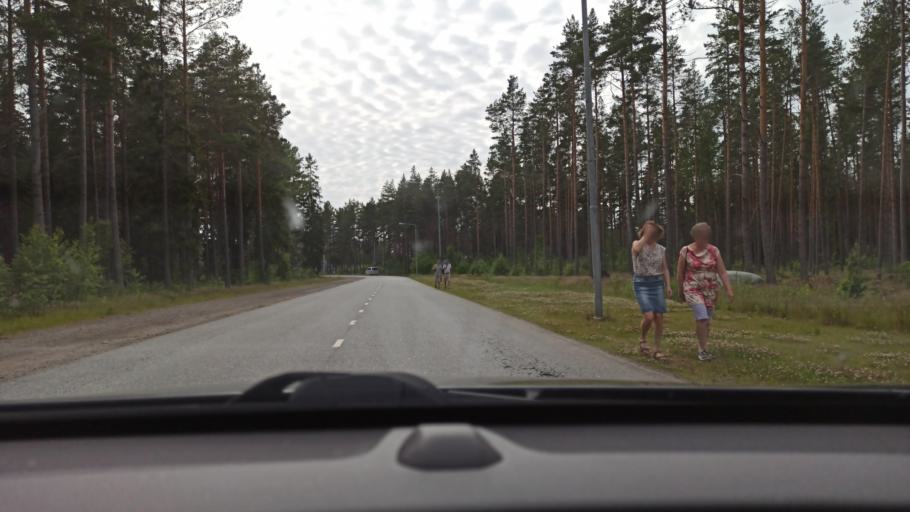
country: FI
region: Satakunta
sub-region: Pori
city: Luvia
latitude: 61.5735
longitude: 21.5216
